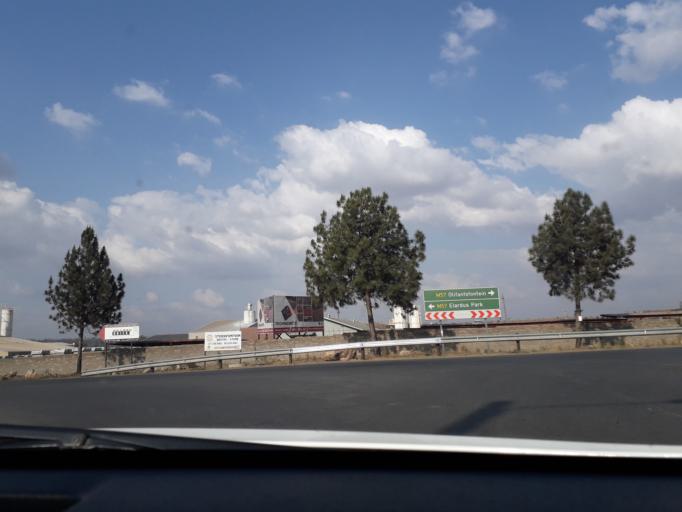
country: ZA
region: Gauteng
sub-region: Ekurhuleni Metropolitan Municipality
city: Tembisa
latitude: -25.9409
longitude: 28.2434
